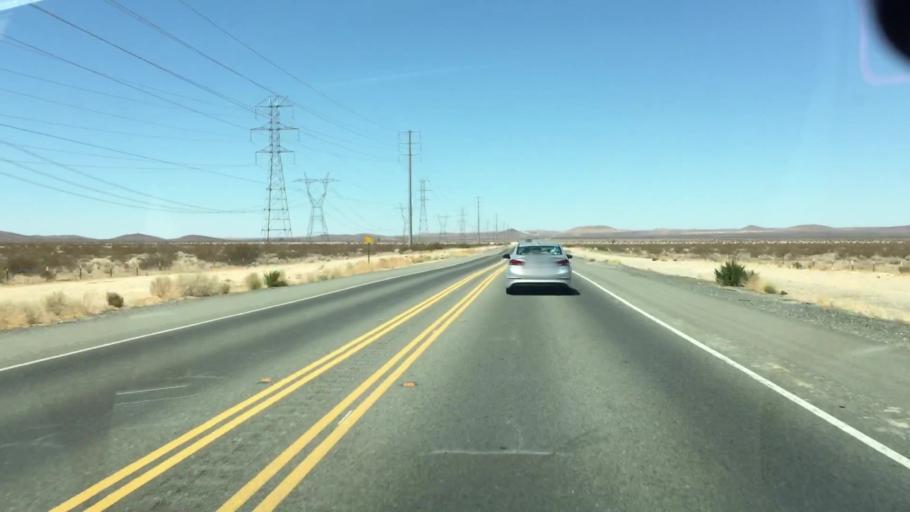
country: US
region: California
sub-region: San Bernardino County
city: Adelanto
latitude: 34.7808
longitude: -117.4808
